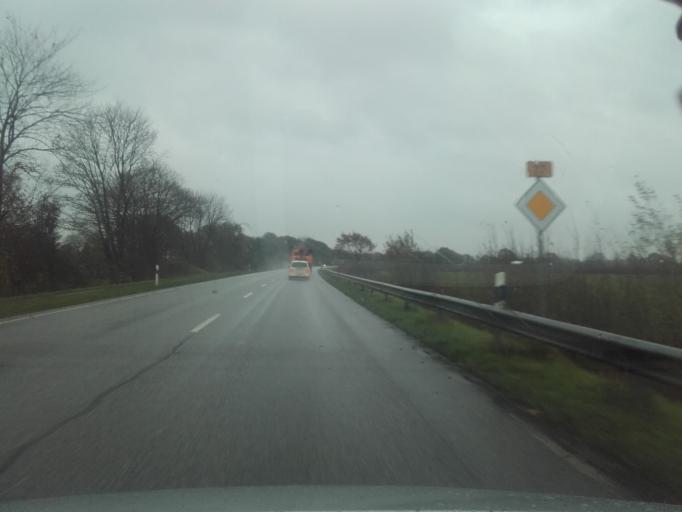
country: DE
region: Schleswig-Holstein
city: Fockbek
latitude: 54.3376
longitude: 9.6107
